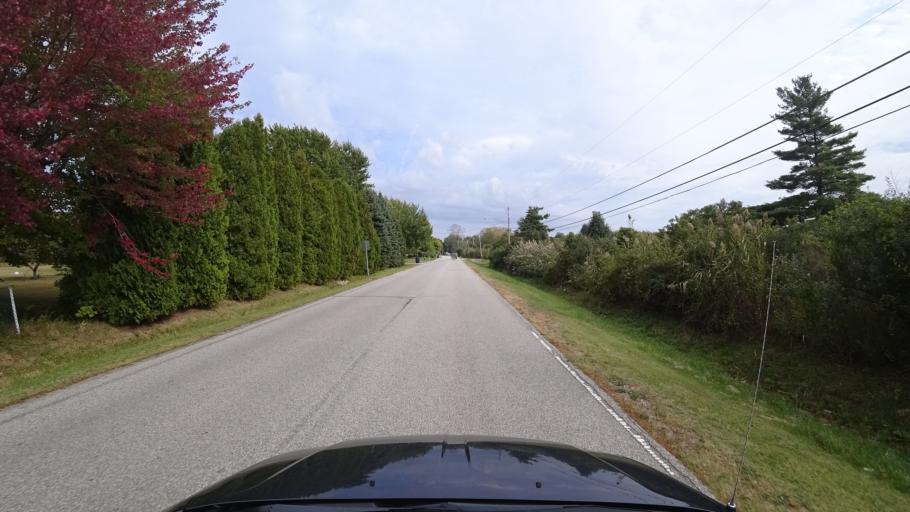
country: US
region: Indiana
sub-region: LaPorte County
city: Long Beach
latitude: 41.7235
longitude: -86.8200
